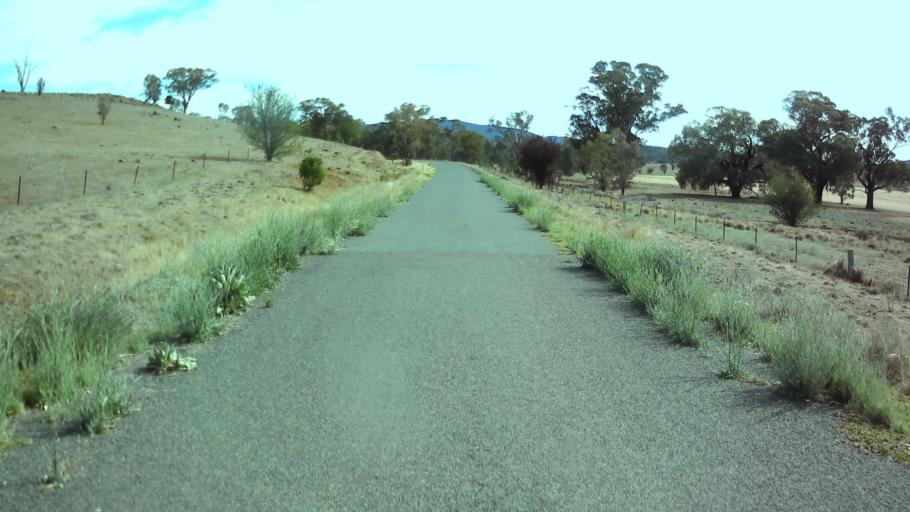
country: AU
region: New South Wales
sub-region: Weddin
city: Grenfell
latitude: -33.8188
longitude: 148.2908
